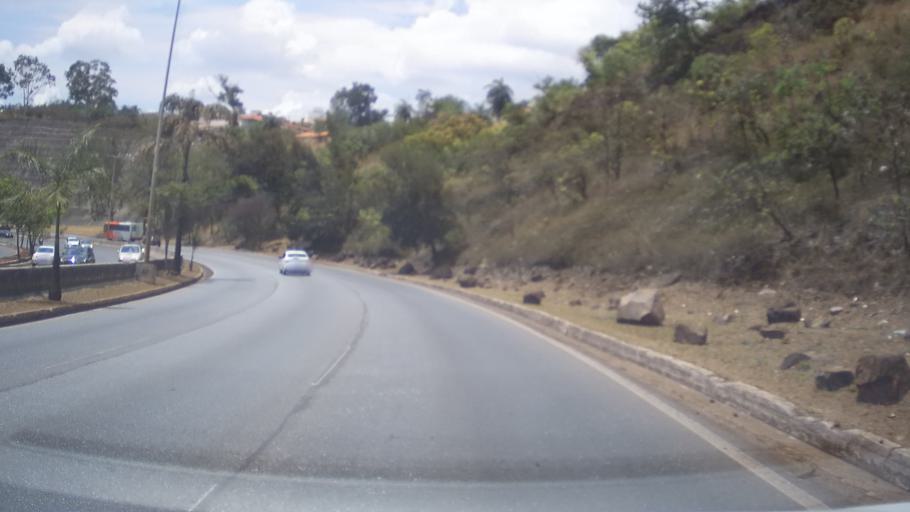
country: BR
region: Minas Gerais
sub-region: Belo Horizonte
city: Belo Horizonte
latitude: -19.9656
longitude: -43.9397
